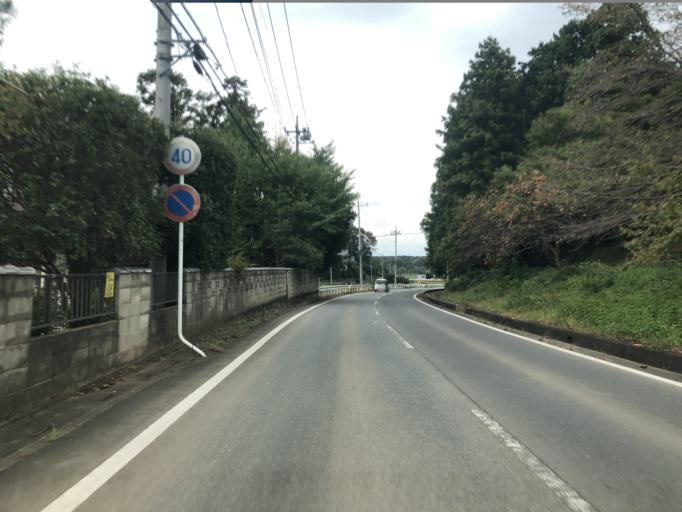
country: JP
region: Saitama
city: Kumagaya
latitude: 36.0681
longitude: 139.3894
